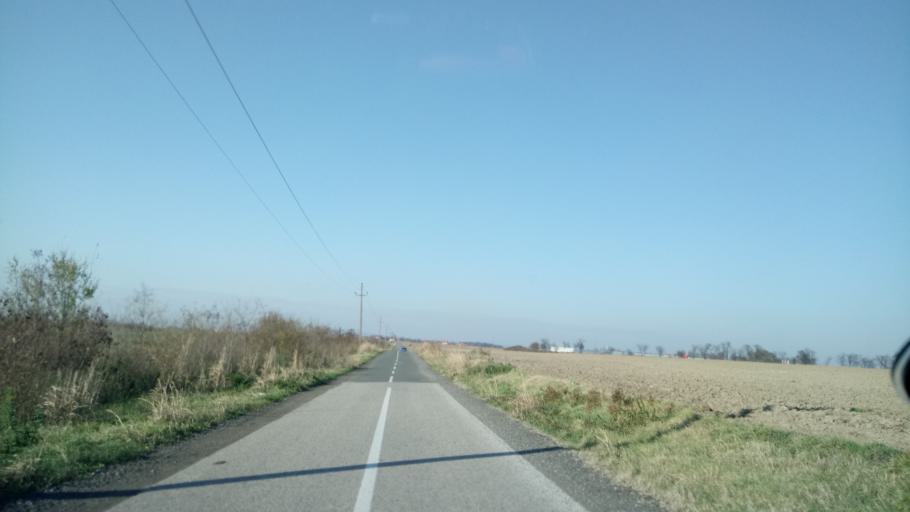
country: RS
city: Ljukovo
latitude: 45.0341
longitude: 20.0439
